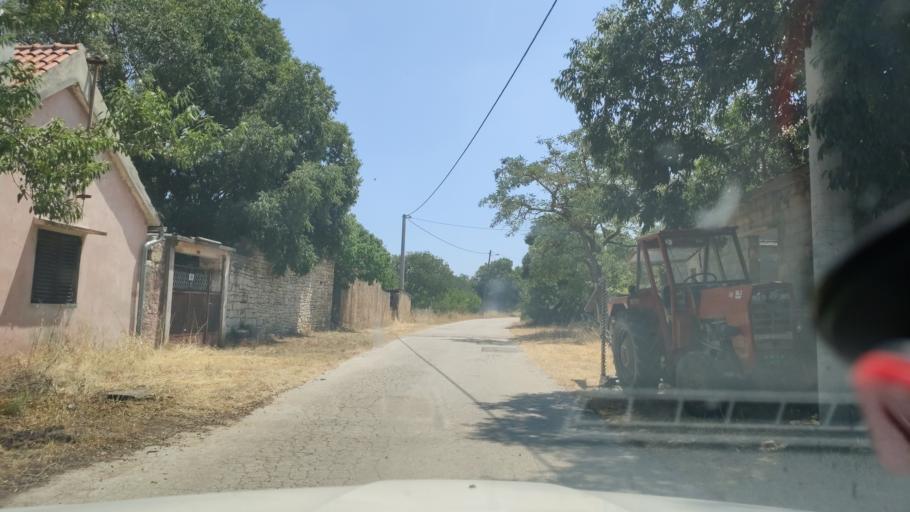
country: HR
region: Sibensko-Kniniska
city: Kistanje
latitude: 43.9567
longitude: 15.8776
